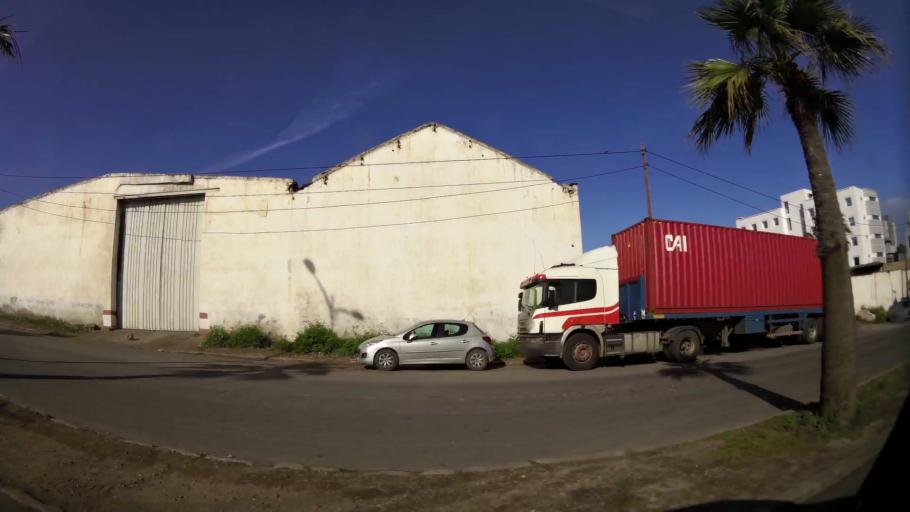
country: MA
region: Grand Casablanca
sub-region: Casablanca
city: Casablanca
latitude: 33.6048
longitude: -7.5748
